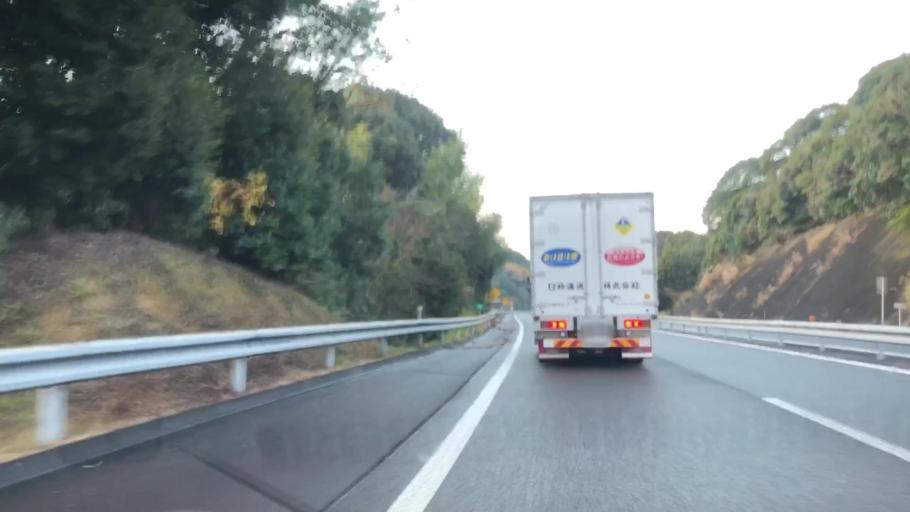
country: JP
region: Nagasaki
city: Sasebo
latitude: 33.1569
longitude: 129.8135
